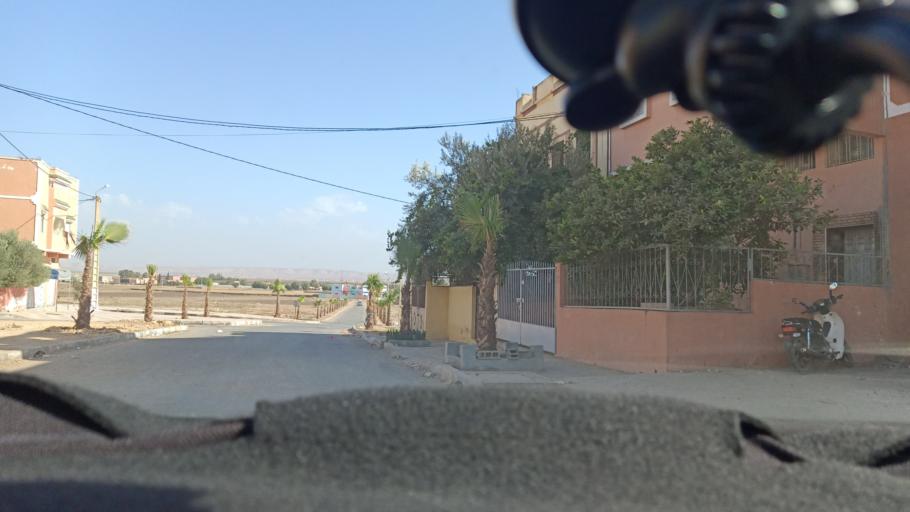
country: MA
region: Doukkala-Abda
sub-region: Safi
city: Youssoufia
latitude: 32.3513
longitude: -8.8364
